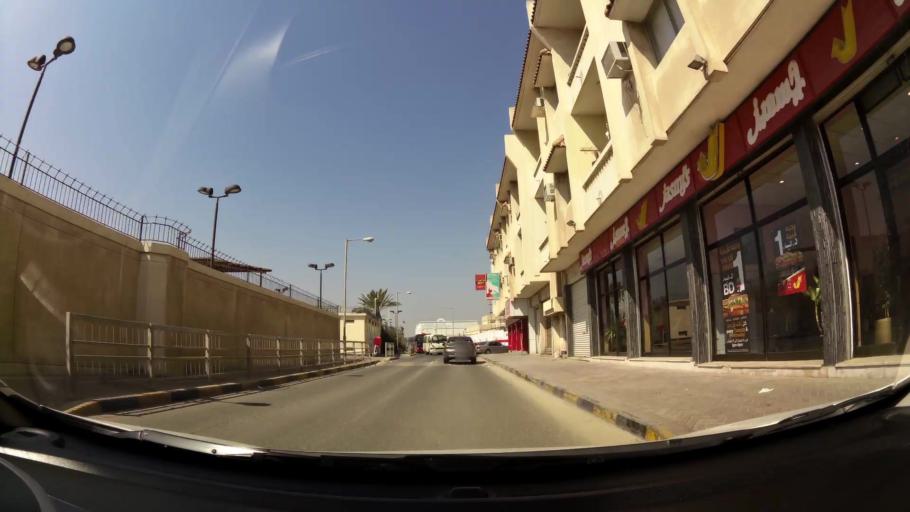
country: BH
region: Manama
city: Manama
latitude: 26.2099
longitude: 50.6037
